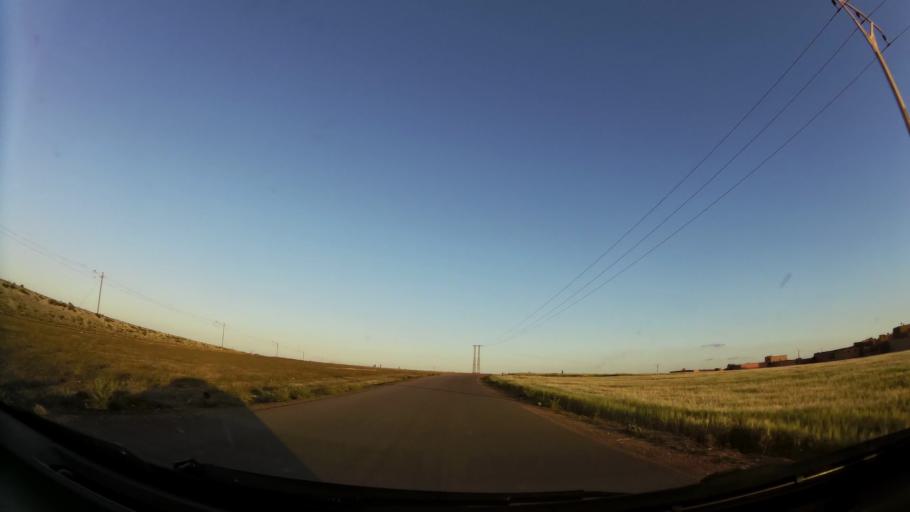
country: MA
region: Marrakech-Tensift-Al Haouz
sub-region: Kelaa-Des-Sraghna
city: Sidi Abdallah
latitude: 32.2394
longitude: -7.9296
